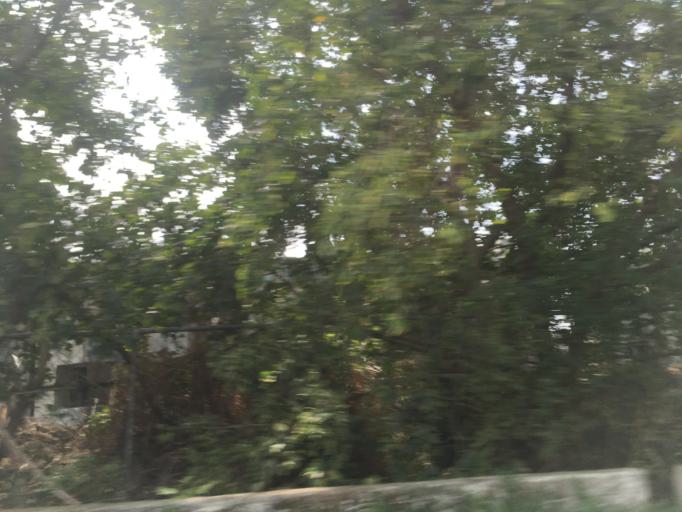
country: TW
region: Taiwan
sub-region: Yunlin
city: Douliu
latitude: 23.6928
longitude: 120.4596
